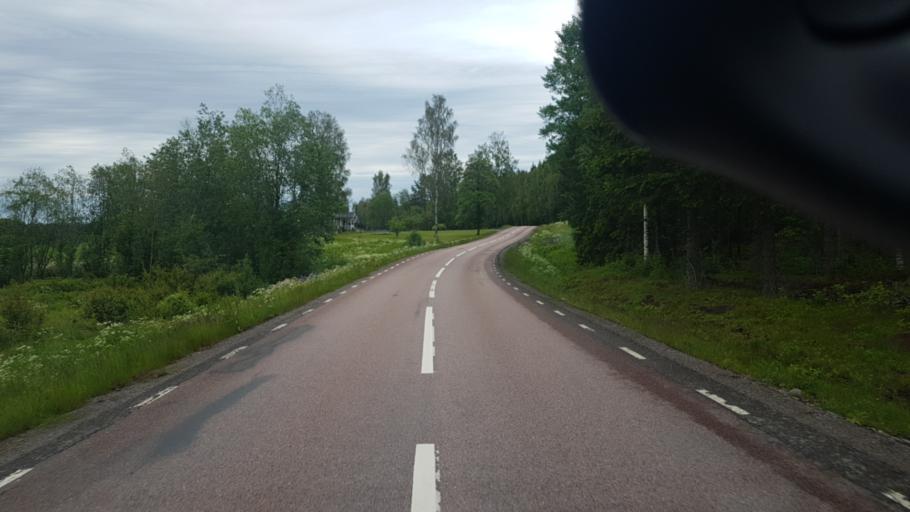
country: SE
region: Vaermland
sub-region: Eda Kommun
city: Amotfors
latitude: 59.7458
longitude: 12.2110
